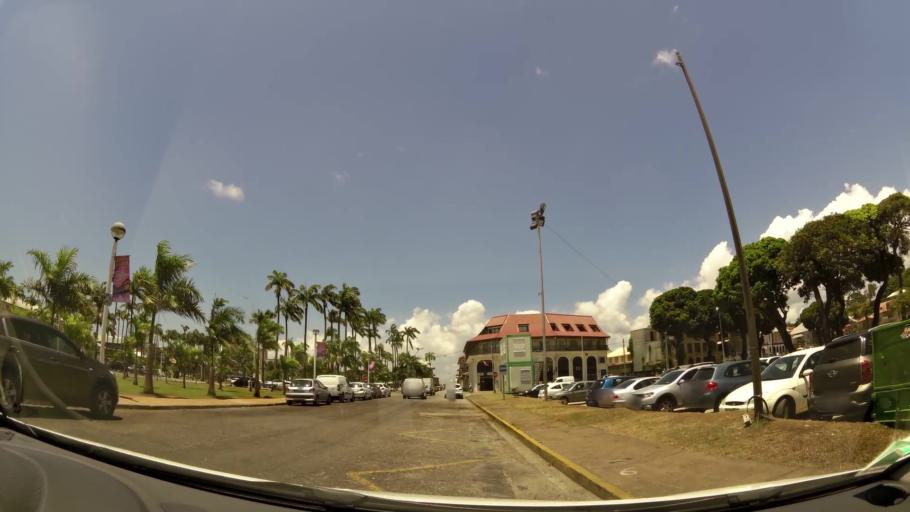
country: GF
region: Guyane
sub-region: Guyane
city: Cayenne
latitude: 4.9401
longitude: -52.3345
